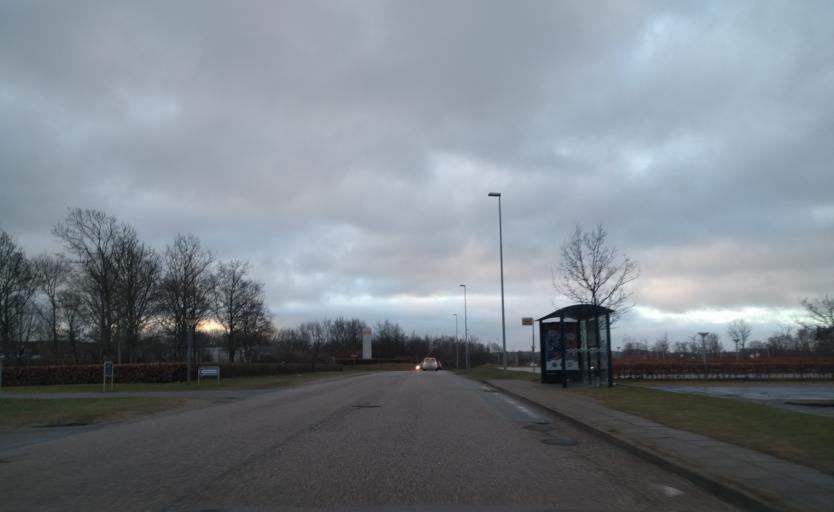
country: DK
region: North Denmark
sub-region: Alborg Kommune
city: Gistrup
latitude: 57.0134
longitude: 9.9841
